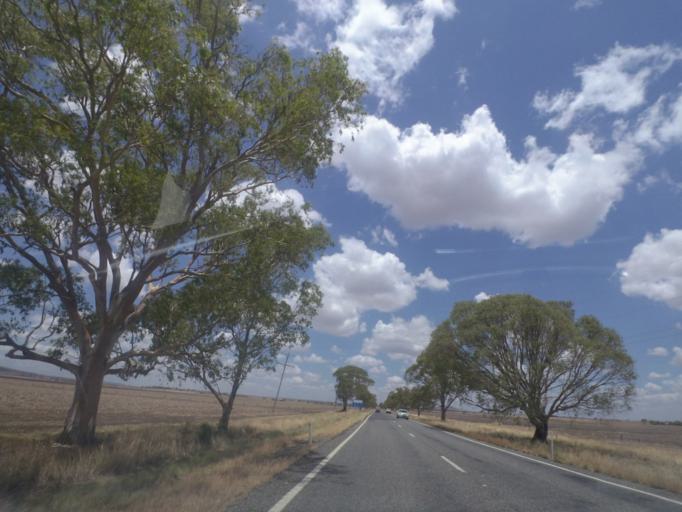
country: AU
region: Queensland
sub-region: Toowoomba
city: Top Camp
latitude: -27.9166
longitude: 151.9814
